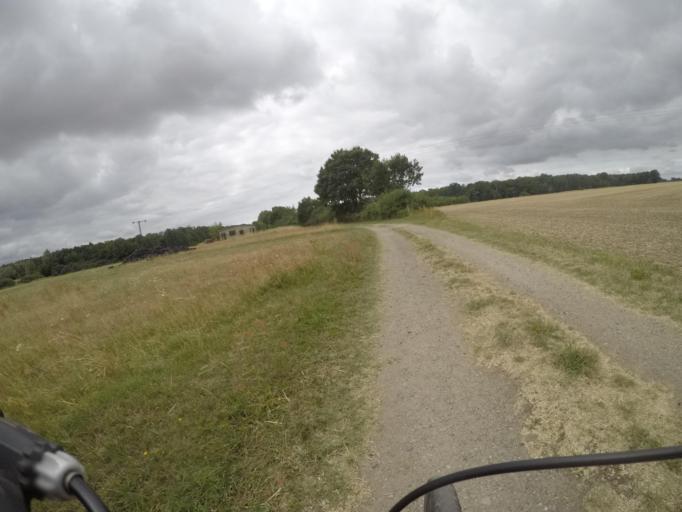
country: DE
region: Lower Saxony
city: Neu Darchau
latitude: 53.2814
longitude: 10.9112
